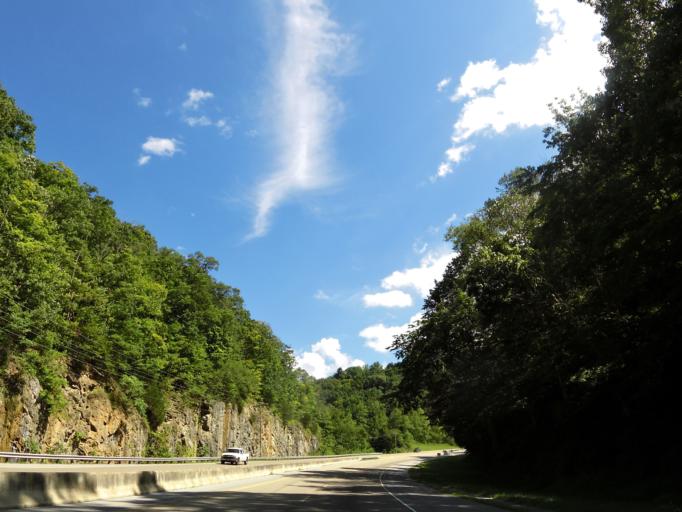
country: US
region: Tennessee
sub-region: Grainger County
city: Rutledge
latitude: 36.3646
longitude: -83.4331
